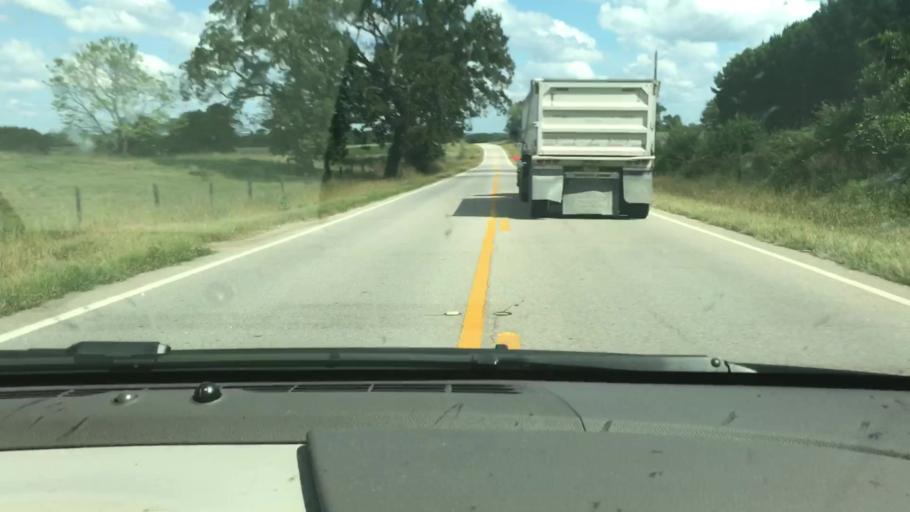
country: US
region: Georgia
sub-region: Troup County
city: West Point
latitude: 32.8791
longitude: -85.0339
